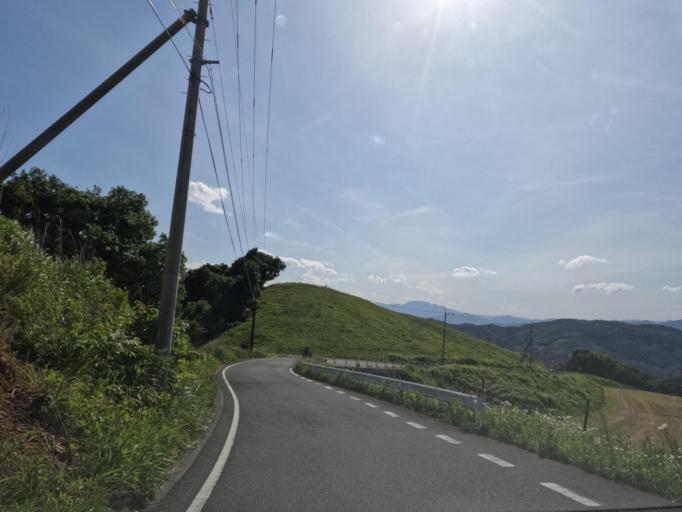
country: JP
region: Saitama
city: Yorii
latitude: 36.0493
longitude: 139.1537
